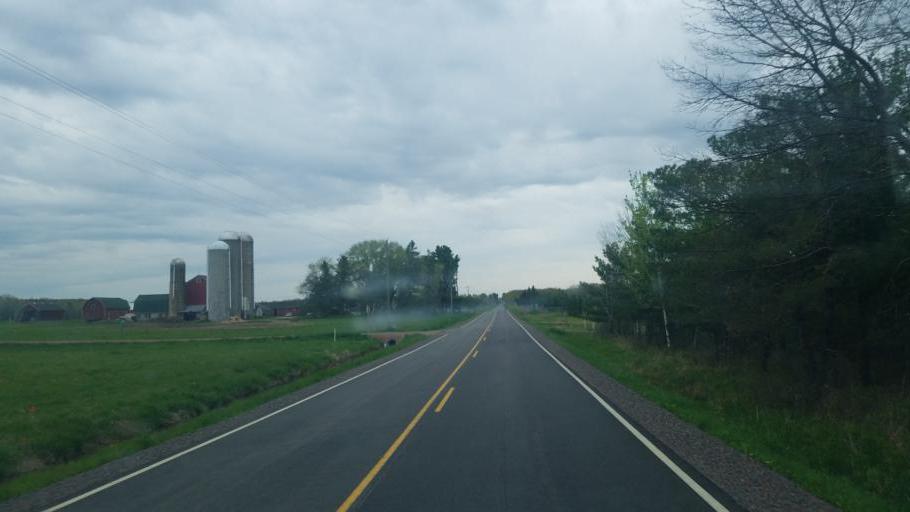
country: US
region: Wisconsin
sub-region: Wood County
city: Marshfield
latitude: 44.4819
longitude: -90.2798
